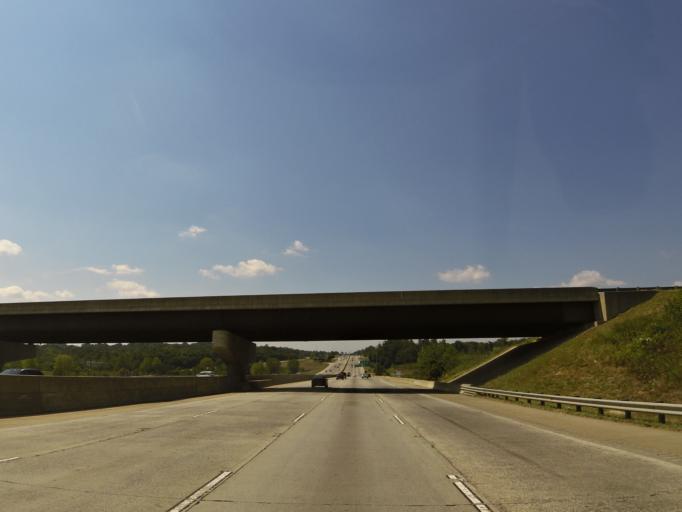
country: US
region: North Carolina
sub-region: Gaston County
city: Mount Holly
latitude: 35.2483
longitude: -80.9663
